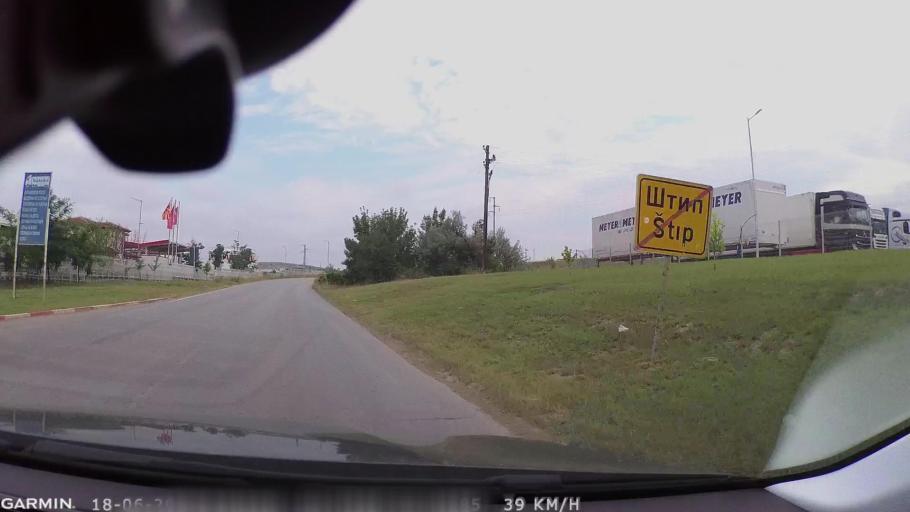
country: MK
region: Stip
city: Shtip
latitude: 41.7721
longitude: 22.1828
